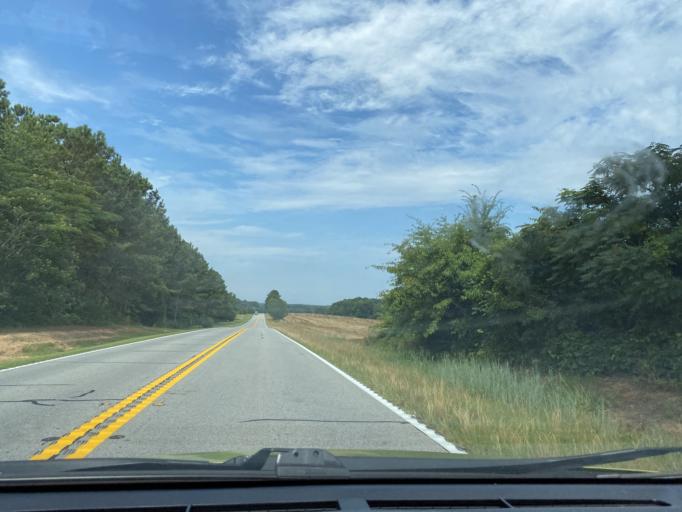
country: US
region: Georgia
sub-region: Coweta County
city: Senoia
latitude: 33.3035
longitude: -84.6627
